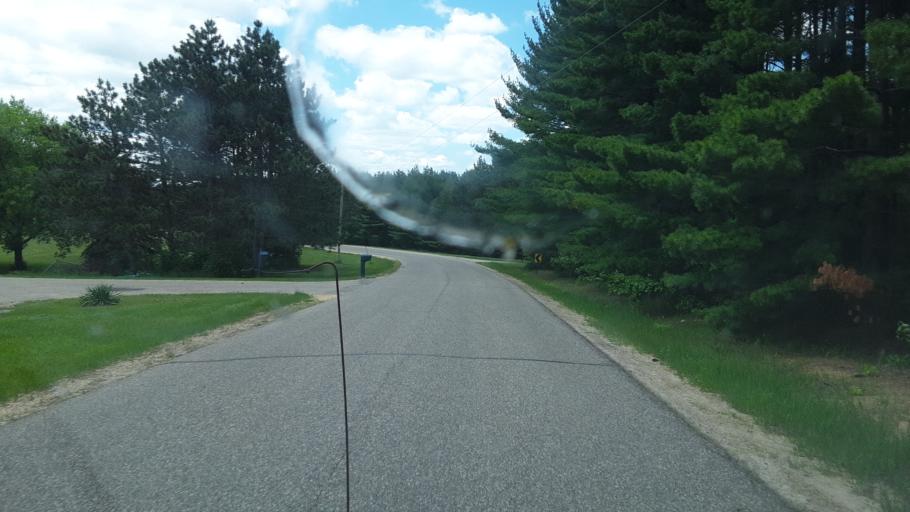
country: US
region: Wisconsin
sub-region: Sauk County
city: Reedsburg
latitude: 43.5625
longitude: -89.9912
